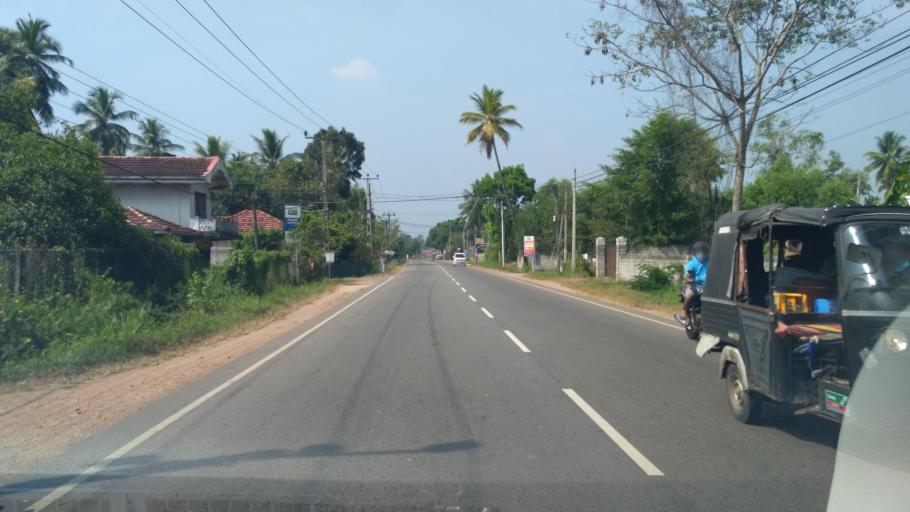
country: LK
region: North Western
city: Kuliyapitiya
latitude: 7.3315
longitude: 79.9996
